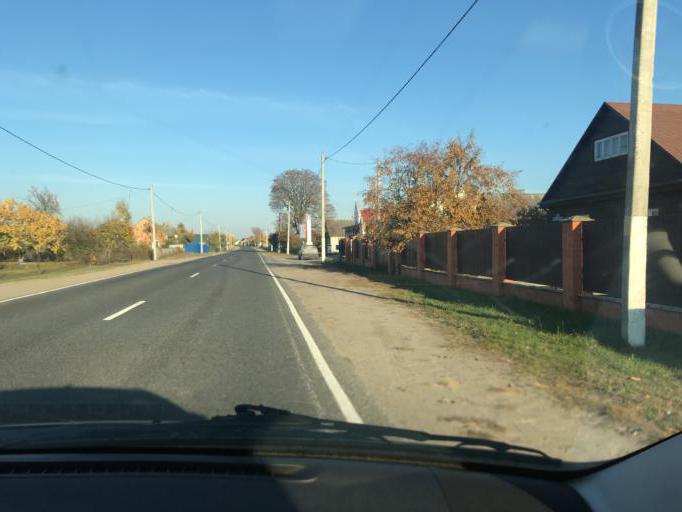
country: BY
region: Brest
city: Stolin
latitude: 51.8325
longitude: 26.7229
